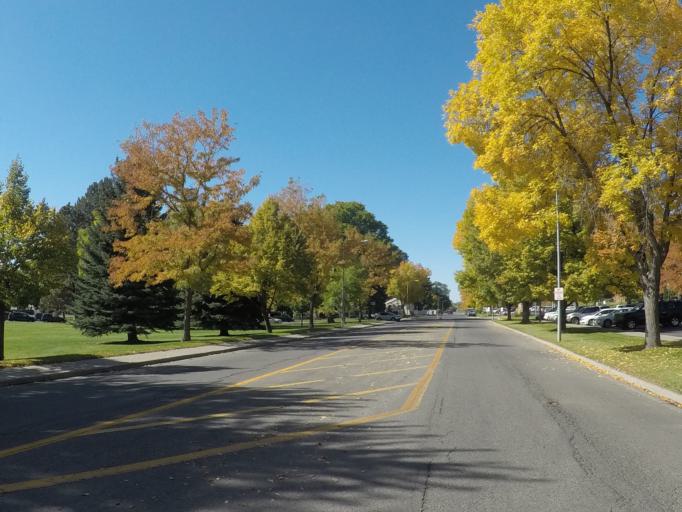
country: US
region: Montana
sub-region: Yellowstone County
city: Billings
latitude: 45.7950
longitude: -108.5203
